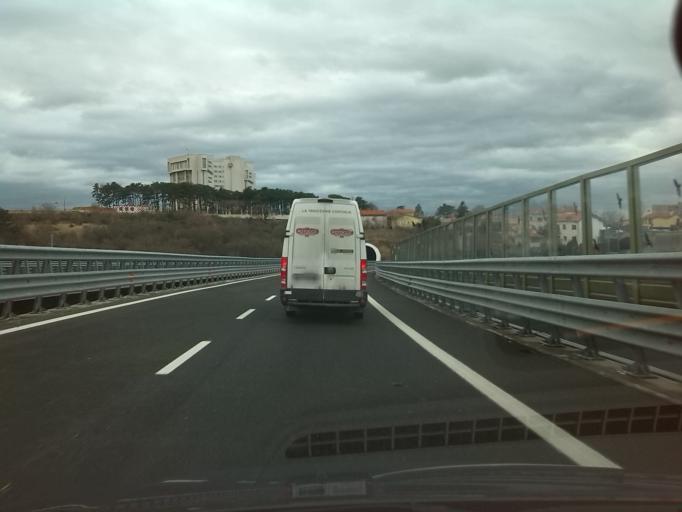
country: IT
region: Friuli Venezia Giulia
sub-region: Provincia di Trieste
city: Domio
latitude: 45.6337
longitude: 13.8340
